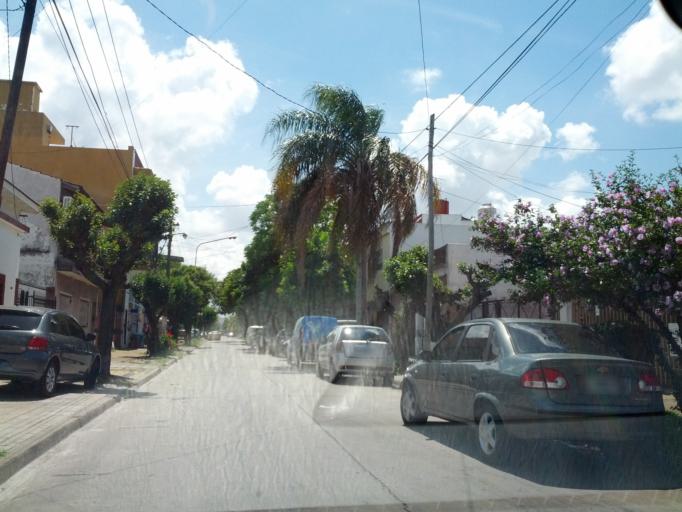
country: AR
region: Buenos Aires
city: San Justo
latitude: -34.6469
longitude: -58.5484
